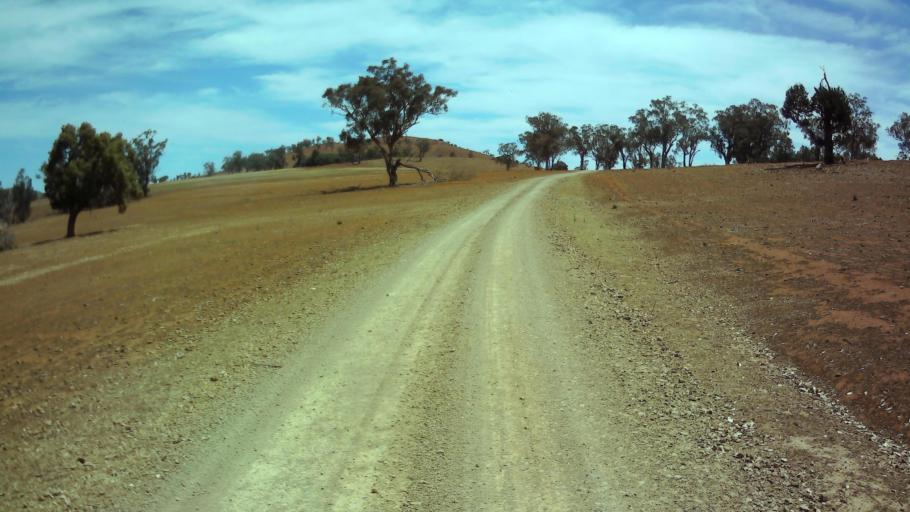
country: AU
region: New South Wales
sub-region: Weddin
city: Grenfell
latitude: -33.7456
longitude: 148.1712
